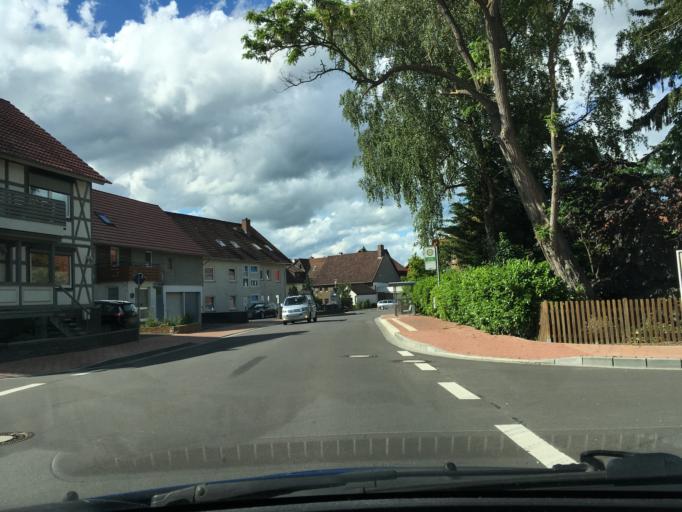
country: DE
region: Lower Saxony
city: Hardegsen
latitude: 51.6175
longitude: 9.8507
